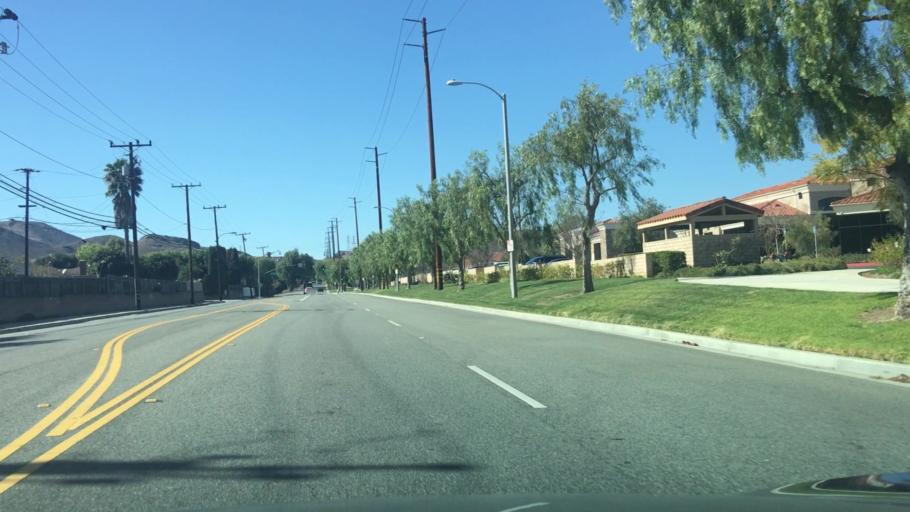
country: US
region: California
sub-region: Ventura County
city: Casa Conejo
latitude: 34.1901
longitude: -118.9427
